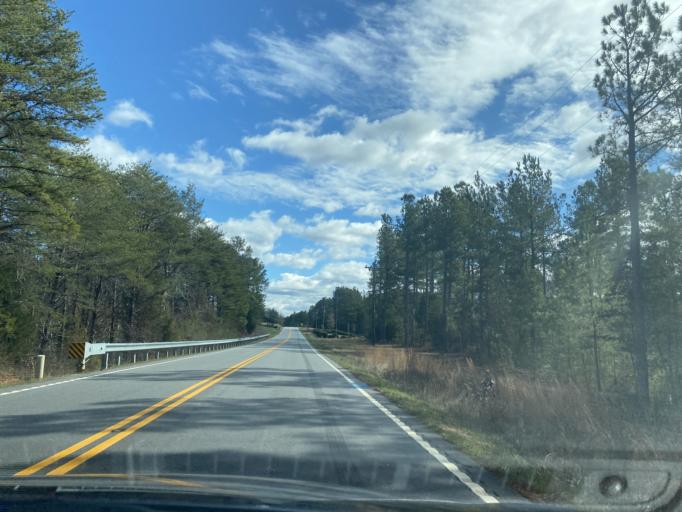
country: US
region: South Carolina
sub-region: Spartanburg County
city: Cowpens
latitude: 35.0951
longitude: -81.7483
